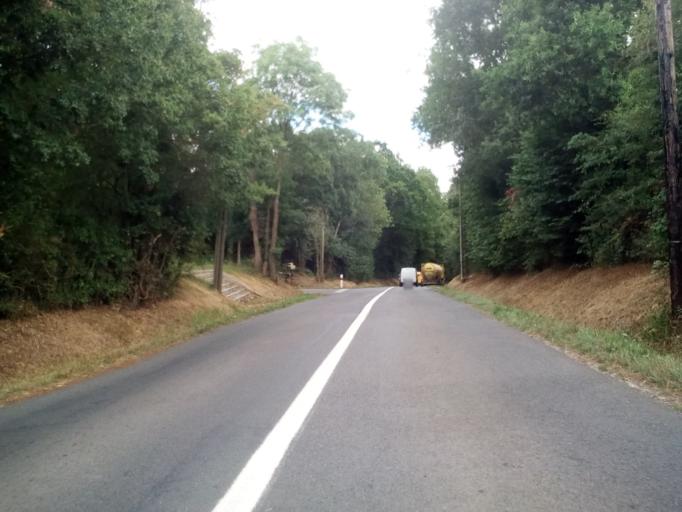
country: FR
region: Lower Normandy
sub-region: Departement du Calvados
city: Troarn
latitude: 49.1554
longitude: -0.1662
